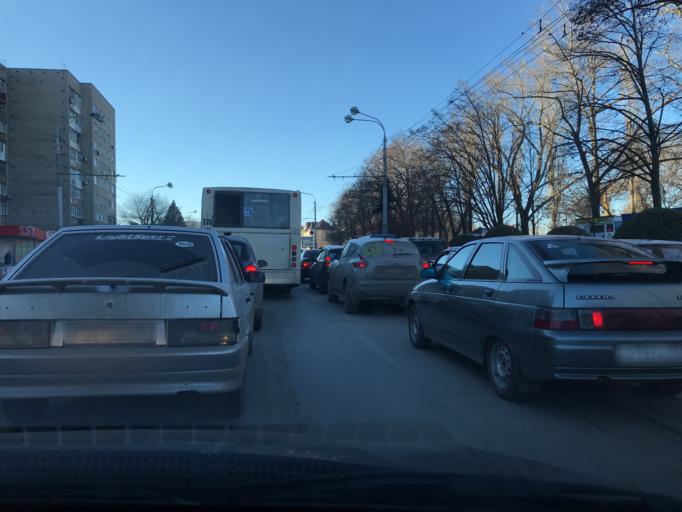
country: RU
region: Rostov
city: Rostov-na-Donu
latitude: 47.2112
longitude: 39.6689
